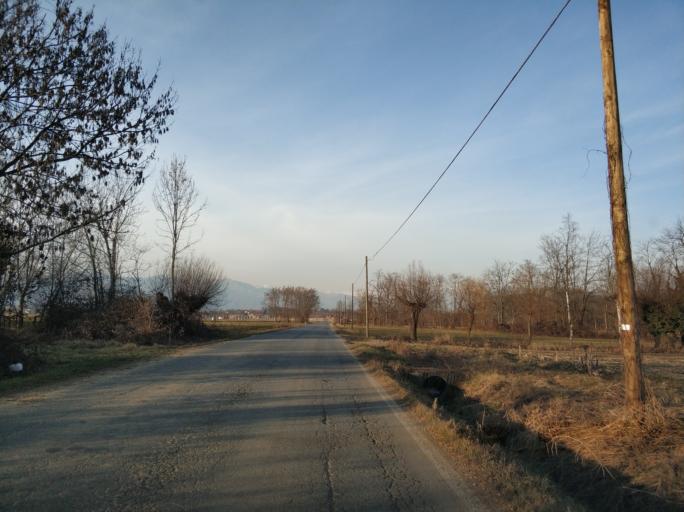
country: IT
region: Piedmont
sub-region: Provincia di Torino
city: San Francesco al Campo
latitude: 45.2134
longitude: 7.6543
